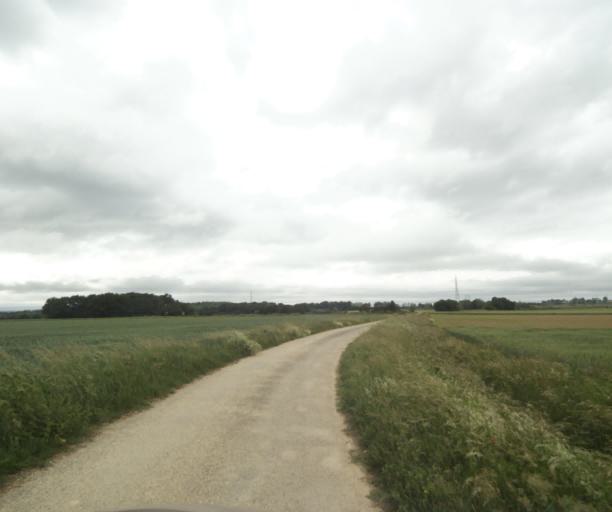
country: FR
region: Rhone-Alpes
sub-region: Departement de l'Ain
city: Tramoyes
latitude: 45.8524
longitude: 4.9563
